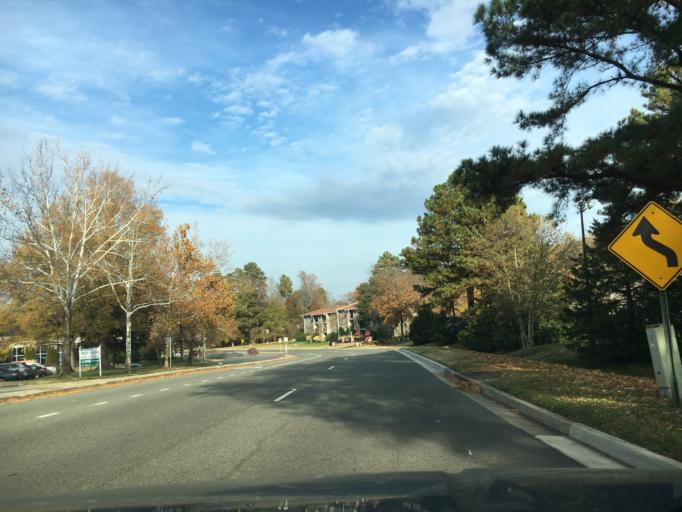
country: US
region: Virginia
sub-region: Henrico County
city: Tuckahoe
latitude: 37.6001
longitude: -77.5453
